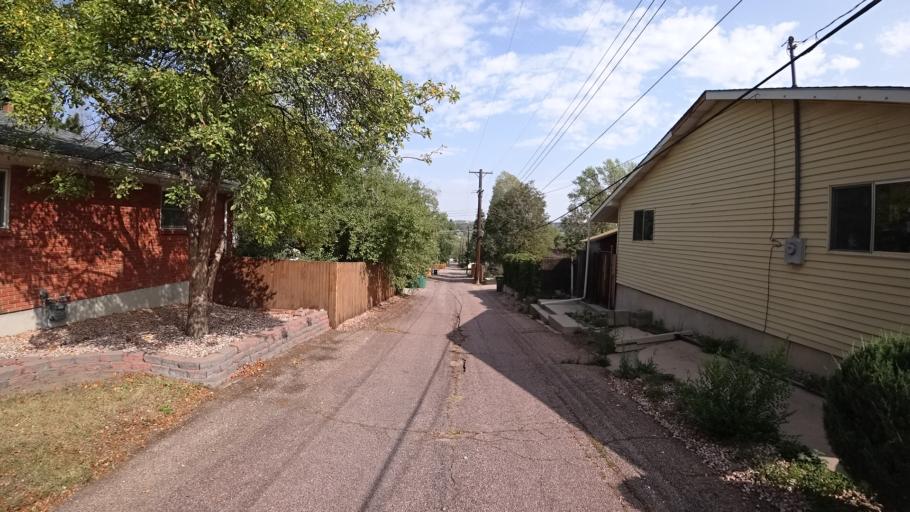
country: US
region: Colorado
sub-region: El Paso County
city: Colorado Springs
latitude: 38.8521
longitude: -104.7918
